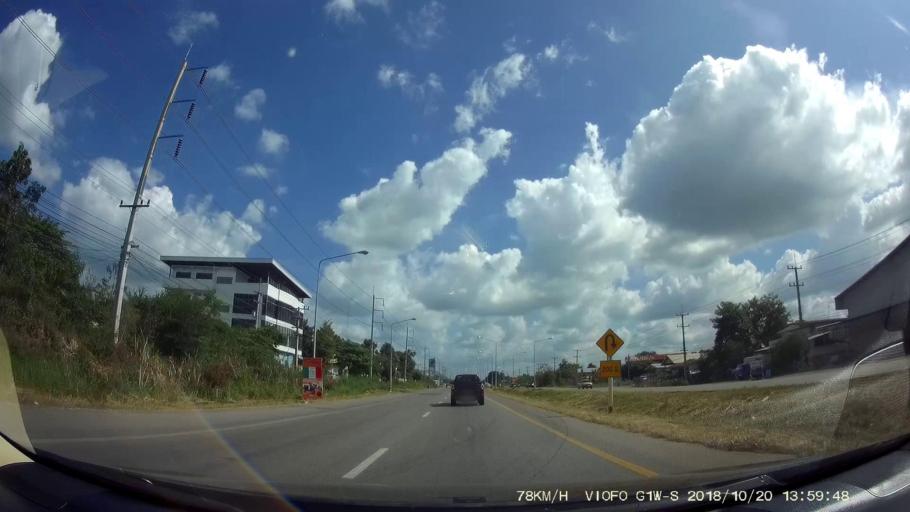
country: TH
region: Khon Kaen
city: Chum Phae
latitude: 16.5212
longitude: 102.1151
